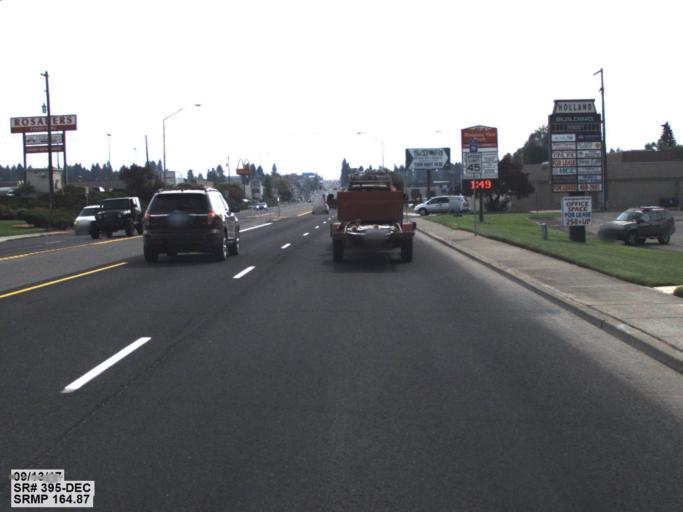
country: US
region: Washington
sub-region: Spokane County
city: Country Homes
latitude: 47.7447
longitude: -117.4115
